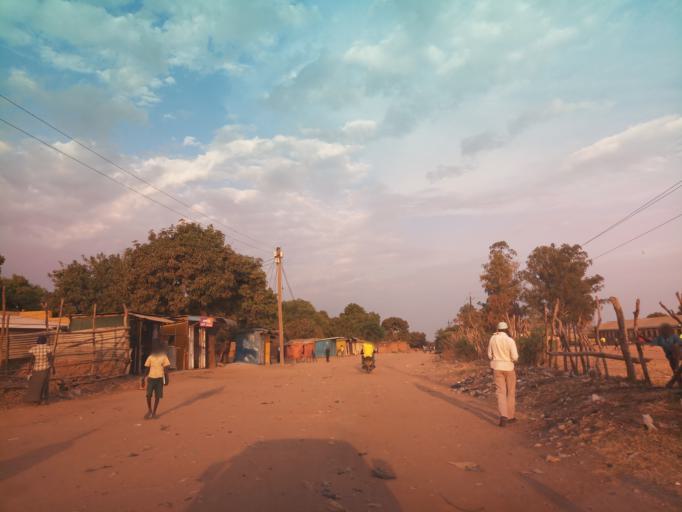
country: UG
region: Northern Region
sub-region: Arua District
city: Arua
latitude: 3.0331
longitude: 30.9137
